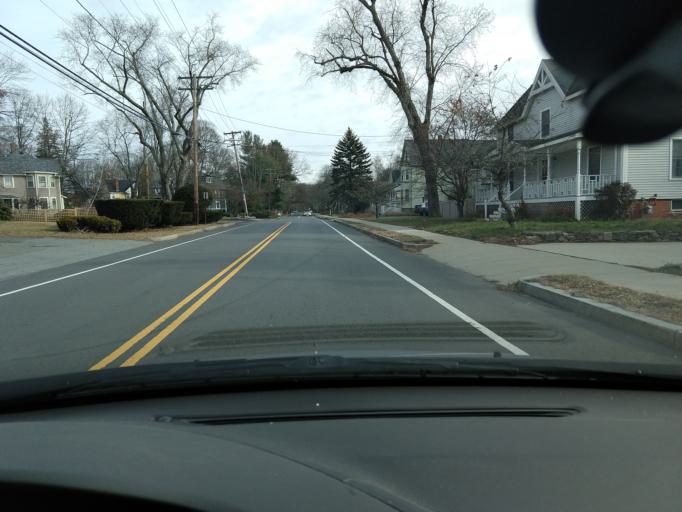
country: US
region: Massachusetts
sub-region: Middlesex County
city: Bedford
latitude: 42.4874
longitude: -71.2750
